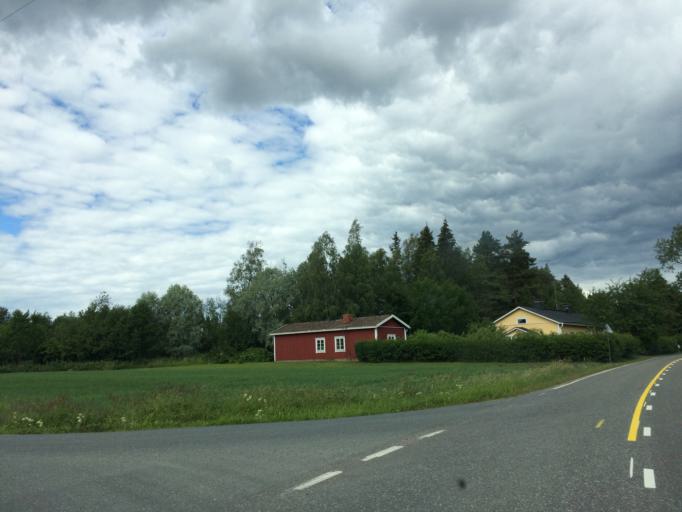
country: FI
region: Haeme
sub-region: Haemeenlinna
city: Tervakoski
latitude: 60.8265
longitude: 24.6191
